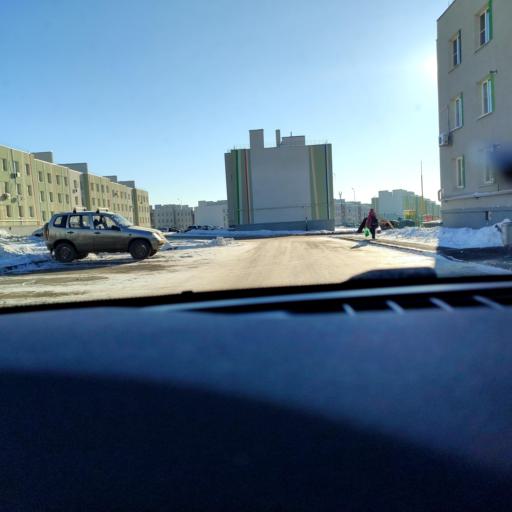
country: RU
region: Samara
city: Petra-Dubrava
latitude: 53.3050
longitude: 50.3427
